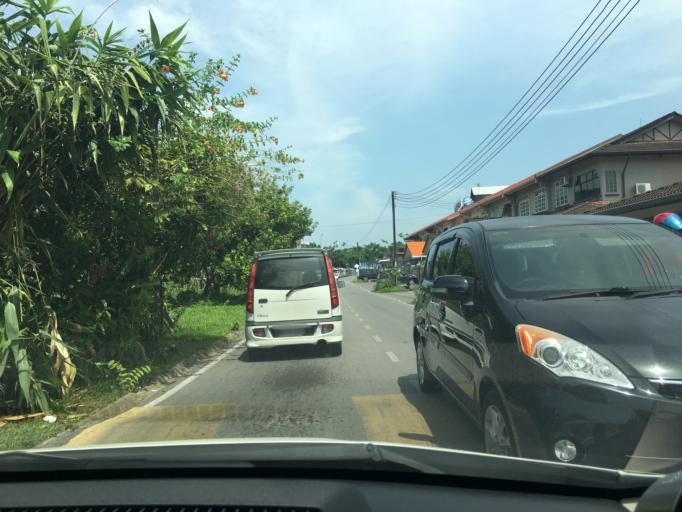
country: MY
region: Sarawak
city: Kuching
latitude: 1.5074
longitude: 110.3018
